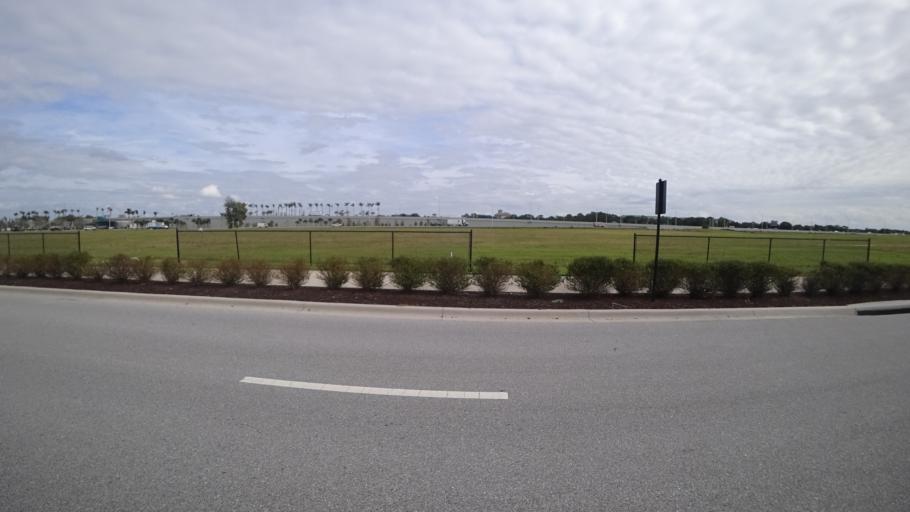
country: US
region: Florida
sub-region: Sarasota County
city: The Meadows
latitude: 27.3859
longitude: -82.4511
